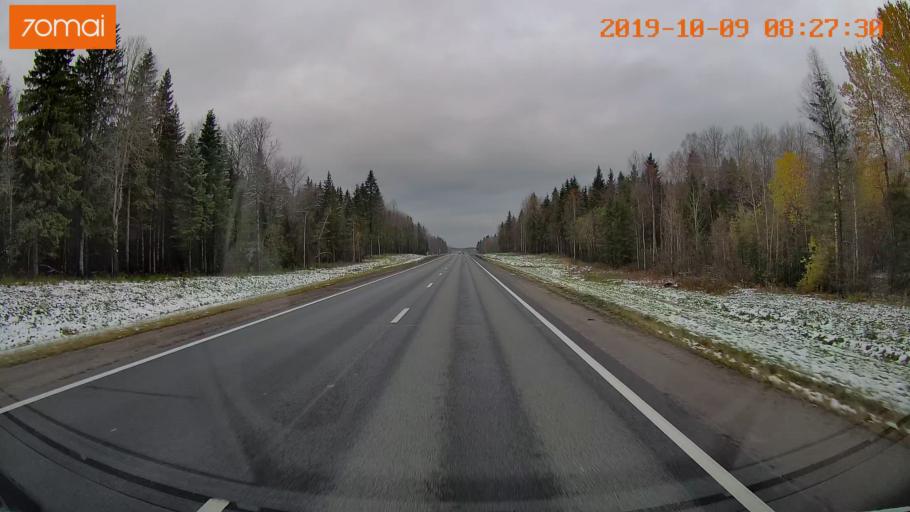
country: RU
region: Vologda
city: Gryazovets
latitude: 58.8047
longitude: 40.2475
